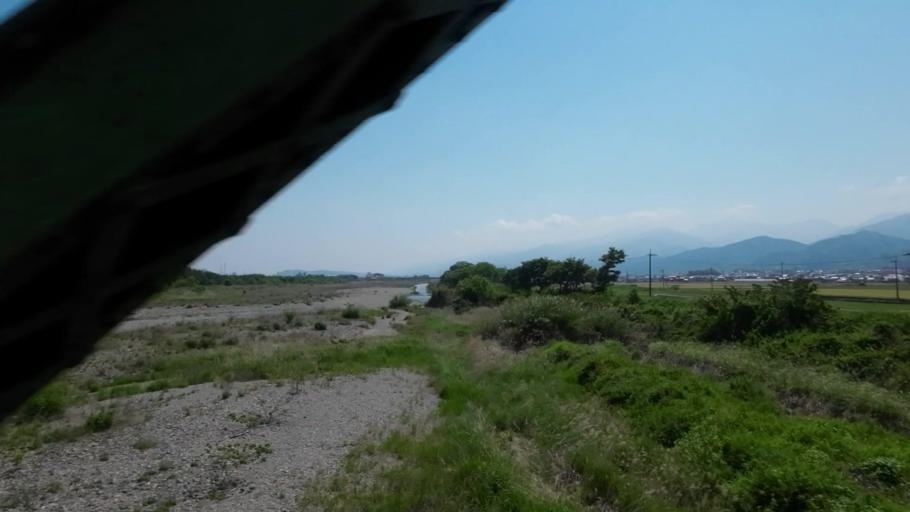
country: JP
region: Ehime
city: Saijo
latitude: 33.9053
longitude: 133.0993
